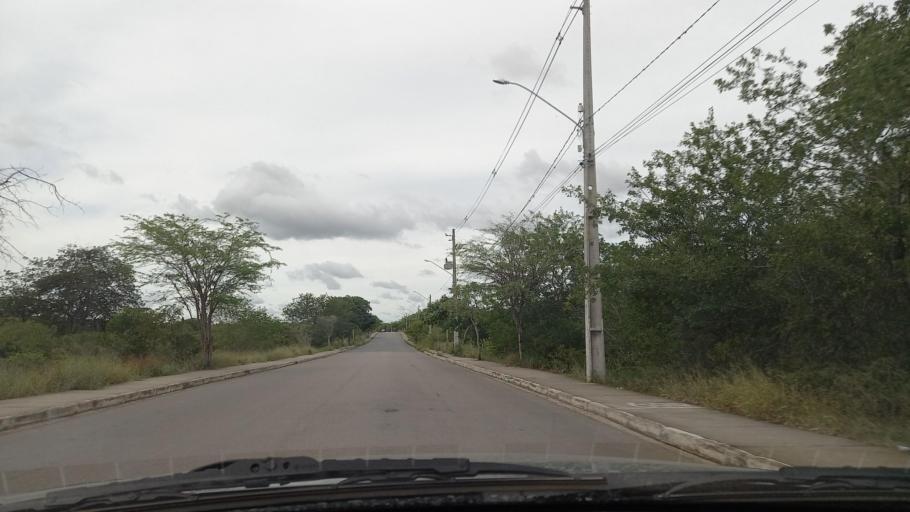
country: BR
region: Pernambuco
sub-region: Gravata
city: Gravata
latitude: -8.2092
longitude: -35.5943
